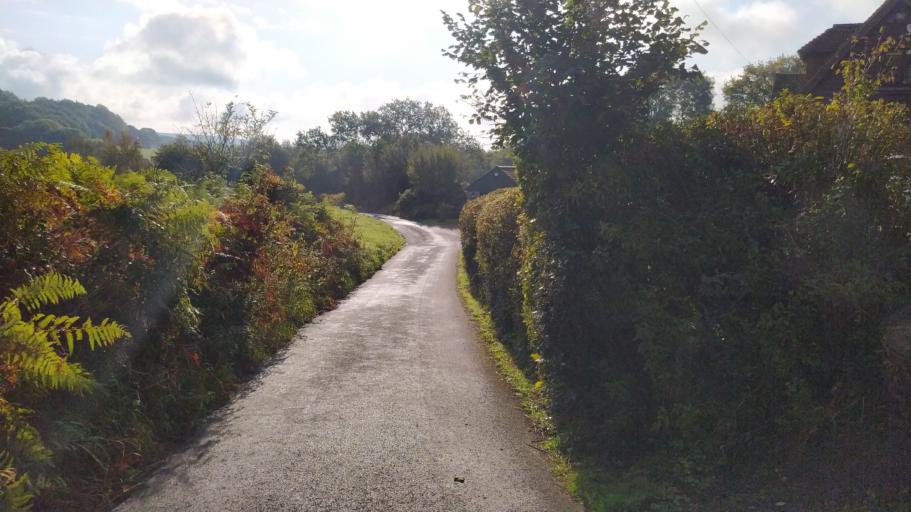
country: GB
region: England
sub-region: Dorset
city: Shaftesbury
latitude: 51.0304
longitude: -2.1475
